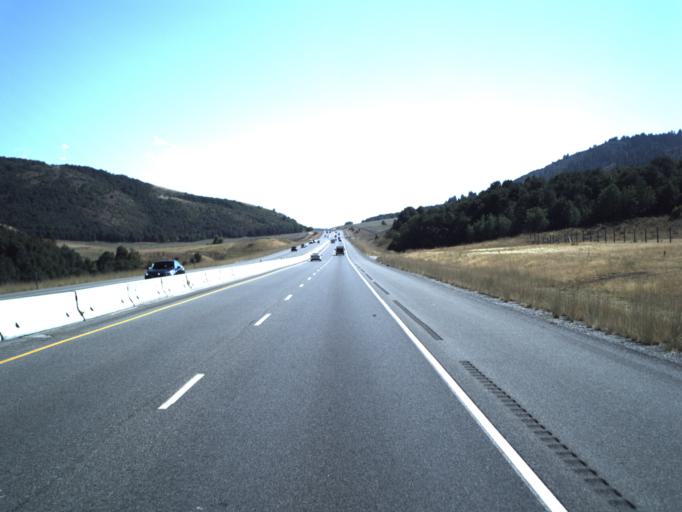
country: US
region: Utah
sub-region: Cache County
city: Wellsville
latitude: 41.5927
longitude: -111.9779
